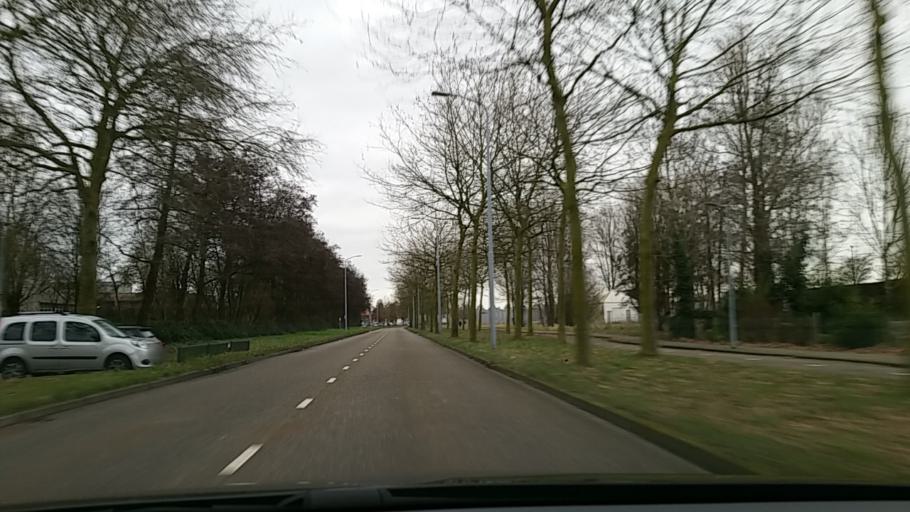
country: NL
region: South Holland
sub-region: Gemeente Kaag en Braassem
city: Leimuiden
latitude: 52.2617
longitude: 4.6436
